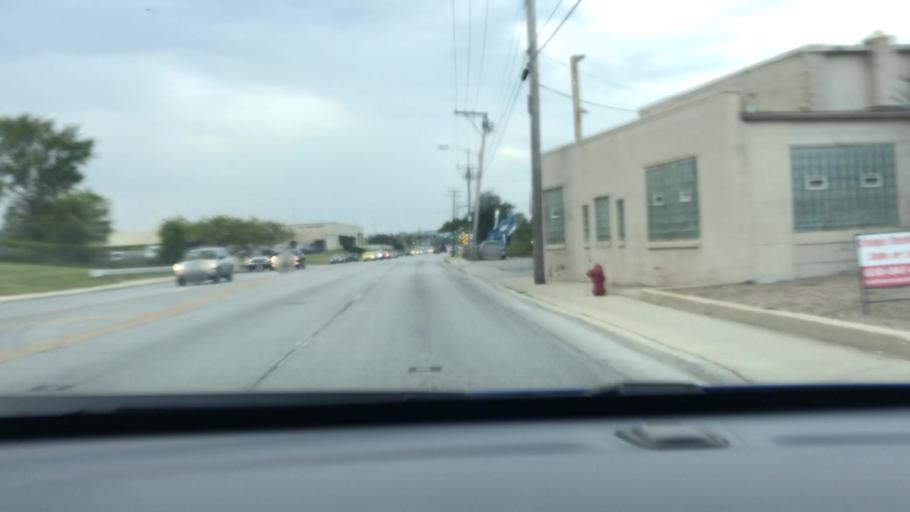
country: US
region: Illinois
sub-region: Kane County
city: Aurora
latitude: 41.7674
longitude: -88.3065
